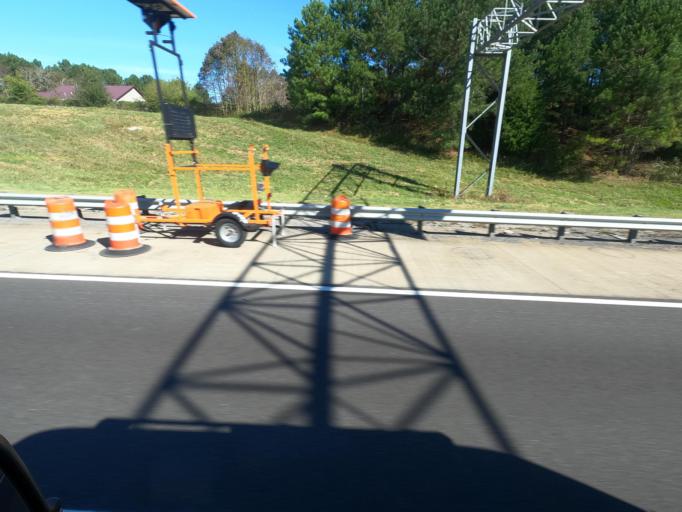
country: US
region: Tennessee
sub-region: Dickson County
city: Burns
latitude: 36.0208
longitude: -87.2608
